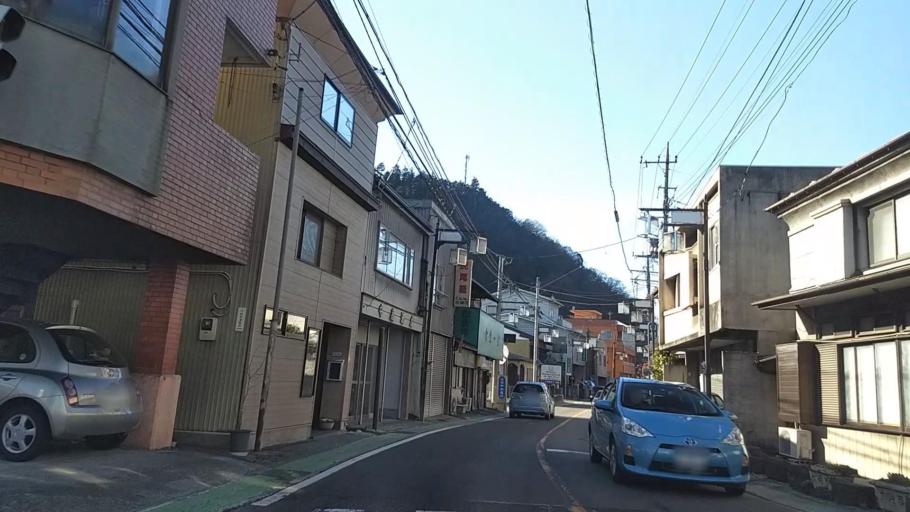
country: JP
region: Yamanashi
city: Otsuki
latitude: 35.6138
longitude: 138.9786
